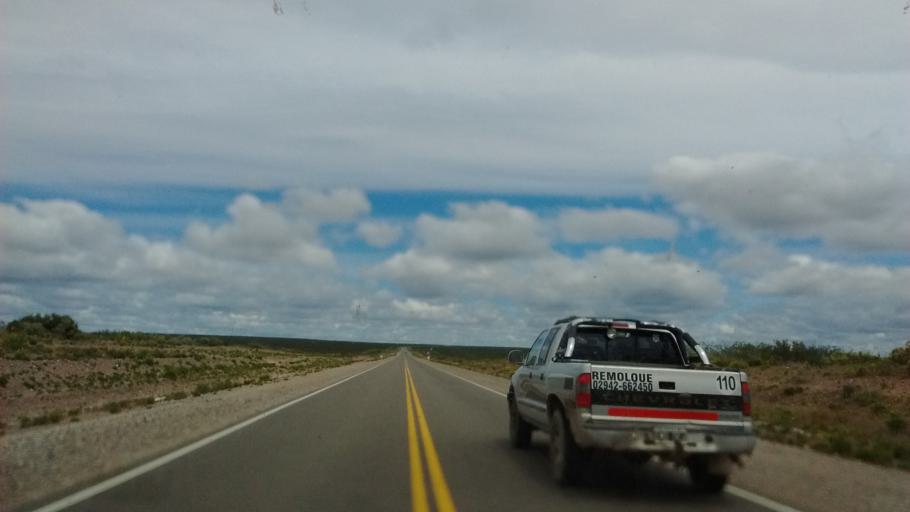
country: AR
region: Neuquen
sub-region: Departamento de Picun Leufu
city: Picun Leufu
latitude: -39.7381
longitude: -69.5953
